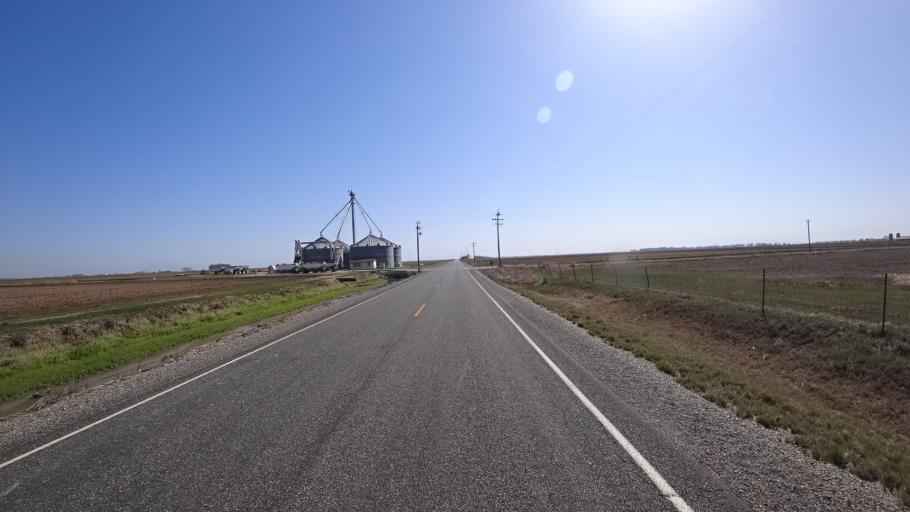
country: US
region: California
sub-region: Glenn County
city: Willows
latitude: 39.4656
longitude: -122.1564
